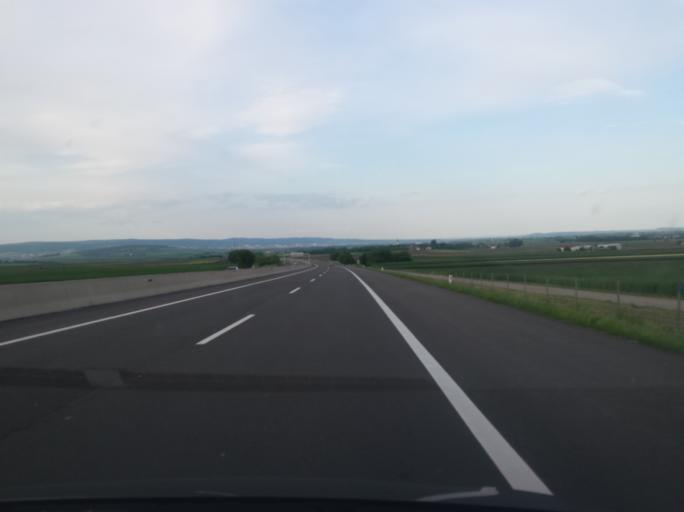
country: AT
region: Burgenland
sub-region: Politischer Bezirk Mattersburg
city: Pottelsdorf
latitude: 47.7621
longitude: 16.4183
